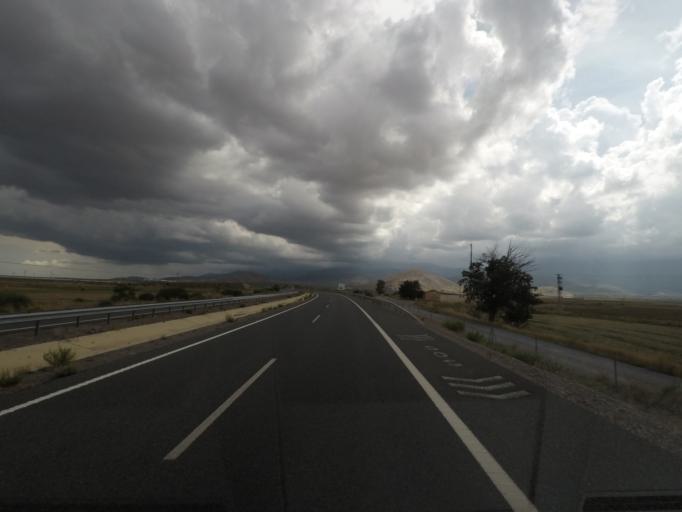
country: ES
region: Andalusia
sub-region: Provincia de Granada
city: Aldeire
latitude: 37.2137
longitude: -3.0711
